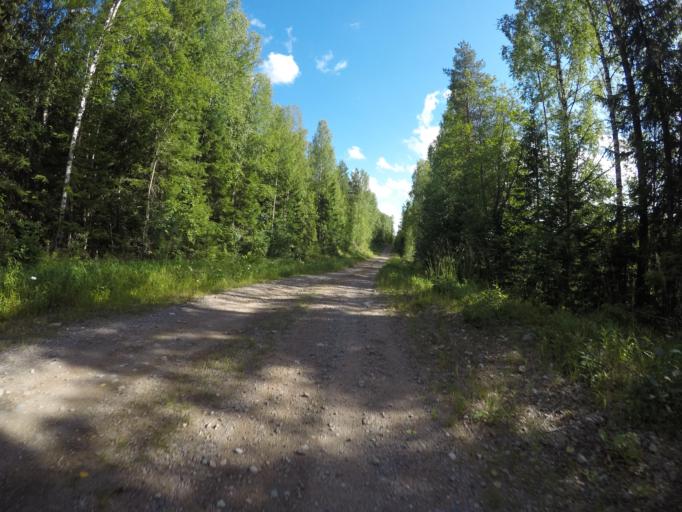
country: SE
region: OErebro
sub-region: Hallefors Kommun
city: Haellefors
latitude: 59.9963
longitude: 14.6055
